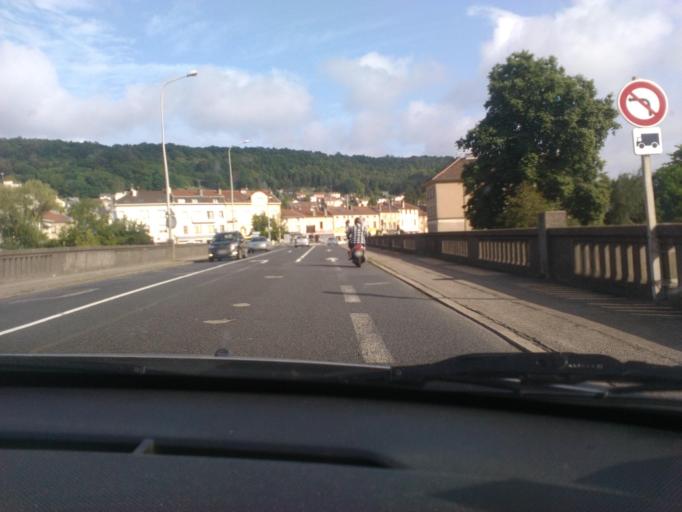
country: FR
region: Lorraine
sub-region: Departement de Meurthe-et-Moselle
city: Frouard
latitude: 48.7658
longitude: 6.1288
